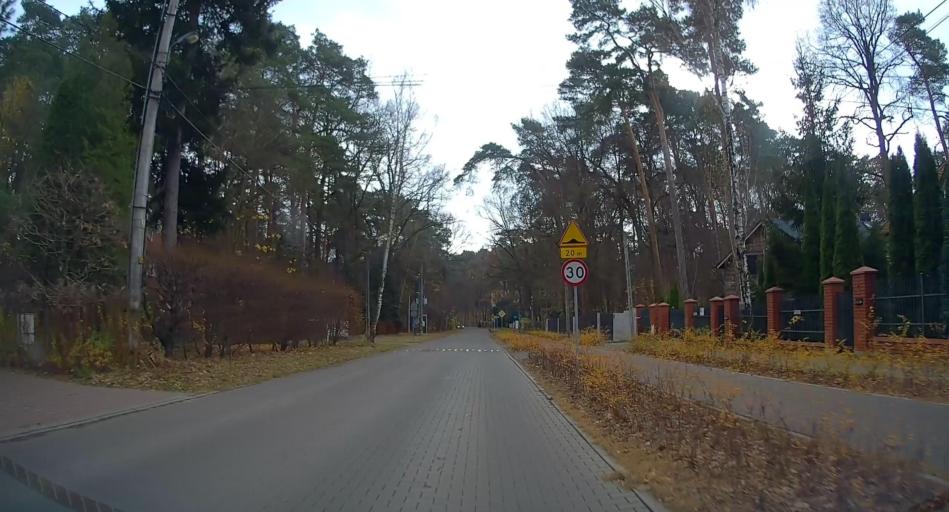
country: PL
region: Masovian Voivodeship
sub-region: Powiat piaseczynski
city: Piaseczno
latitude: 52.0560
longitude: 21.0187
